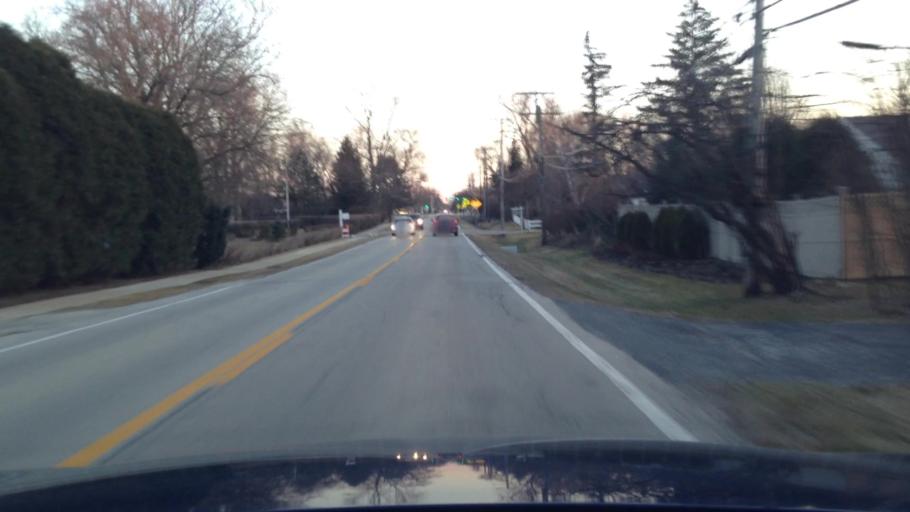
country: US
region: Illinois
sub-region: Cook County
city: Northfield
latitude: 42.1094
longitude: -87.7902
